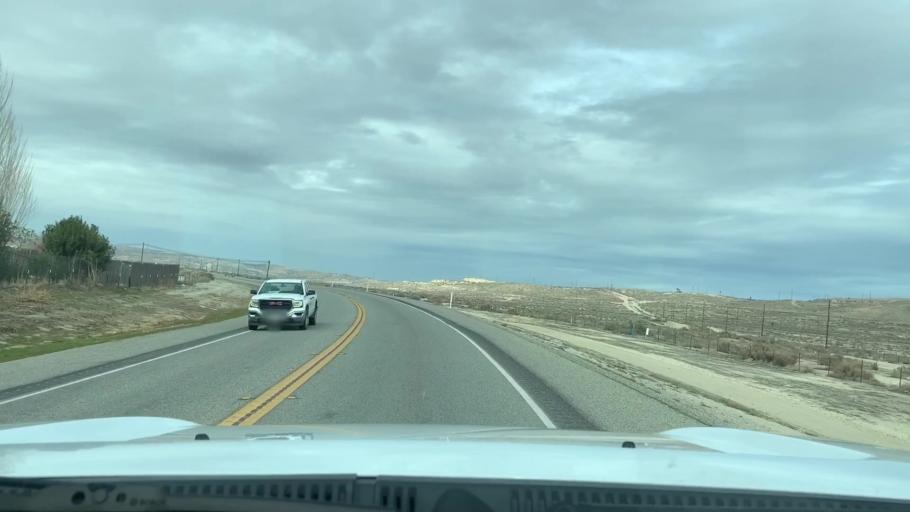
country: US
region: California
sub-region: Kern County
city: Ford City
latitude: 35.1560
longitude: -119.4480
